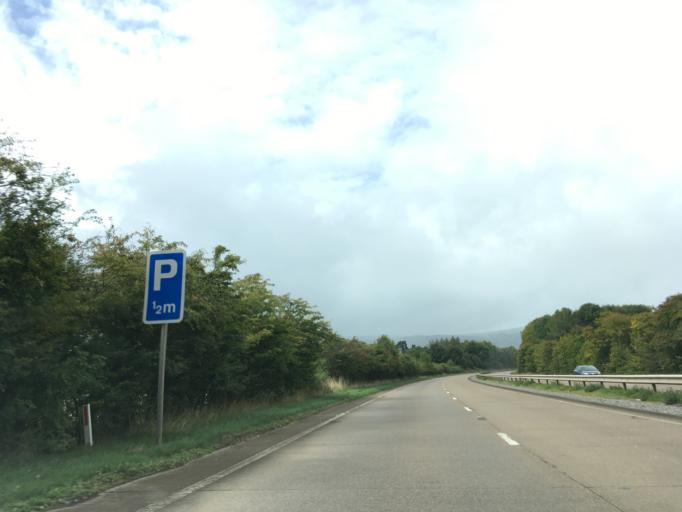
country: GB
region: Wales
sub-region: Monmouthshire
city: Abergavenny
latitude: 51.7845
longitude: -2.9728
